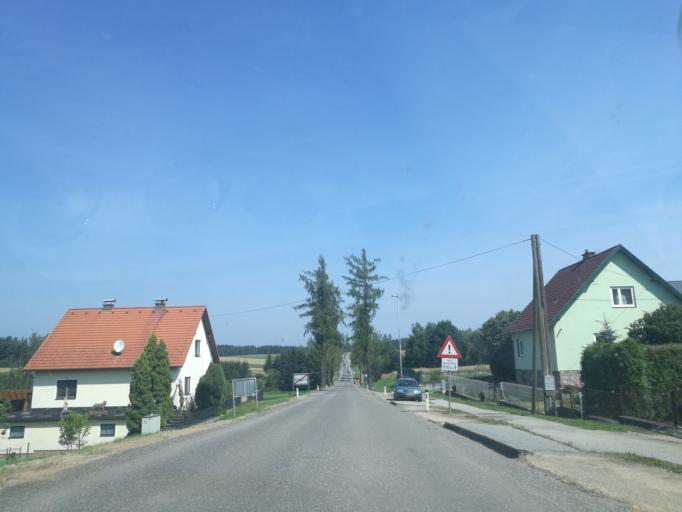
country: AT
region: Lower Austria
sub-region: Politischer Bezirk Gmund
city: Eisgarn
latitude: 48.9175
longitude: 15.1050
